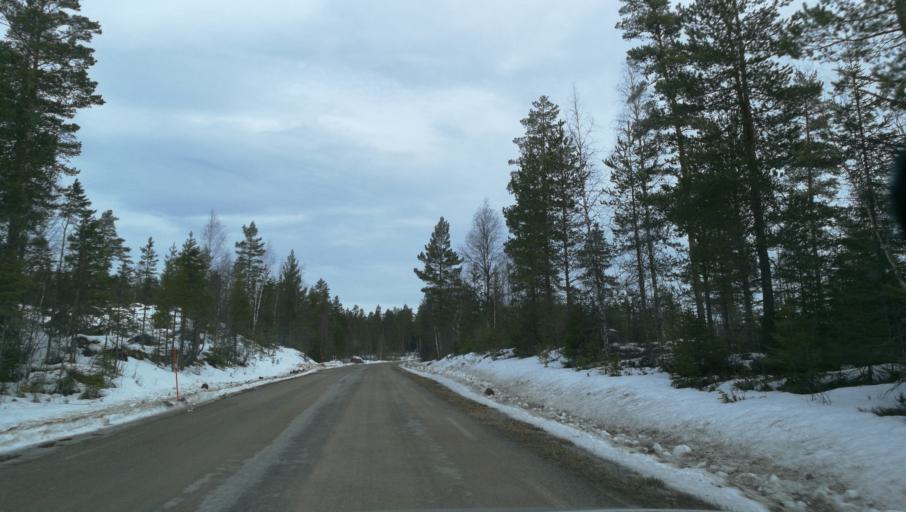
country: NO
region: Hedmark
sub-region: Grue
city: Kirkenaer
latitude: 60.5158
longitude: 12.5530
